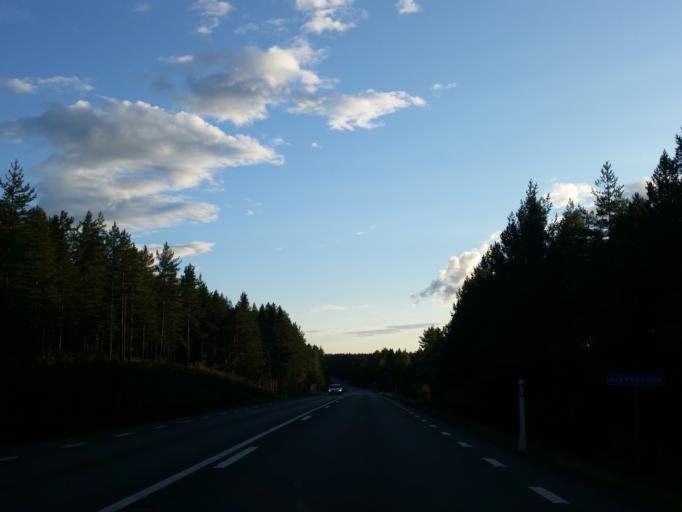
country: SE
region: Vaesterbotten
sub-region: Robertsfors Kommun
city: Robertsfors
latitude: 64.0150
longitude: 20.8247
